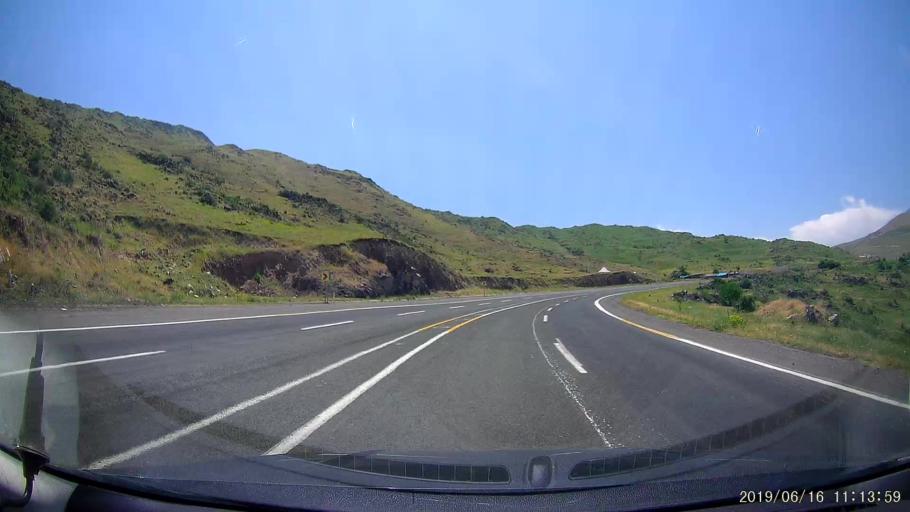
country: TR
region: Igdir
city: Igdir
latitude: 39.7854
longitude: 44.1465
